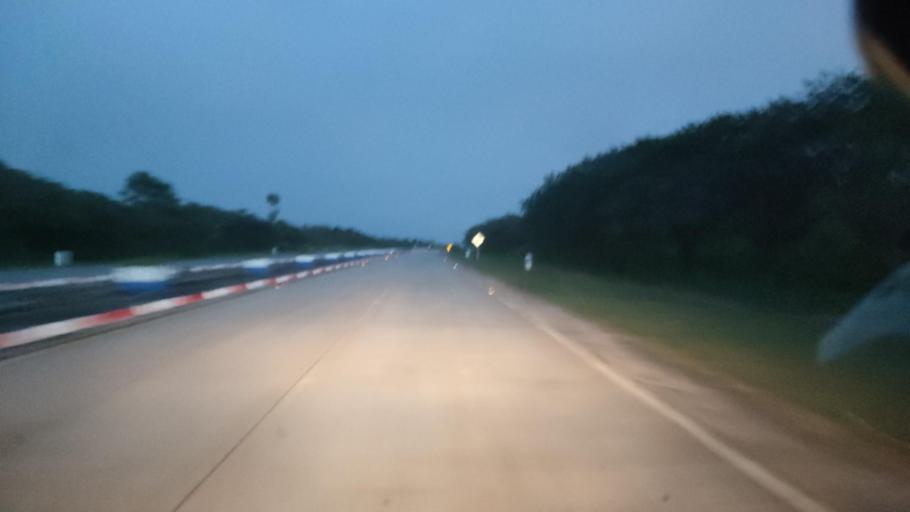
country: MM
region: Mandalay
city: Nay Pyi Taw
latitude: 20.0108
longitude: 95.9563
